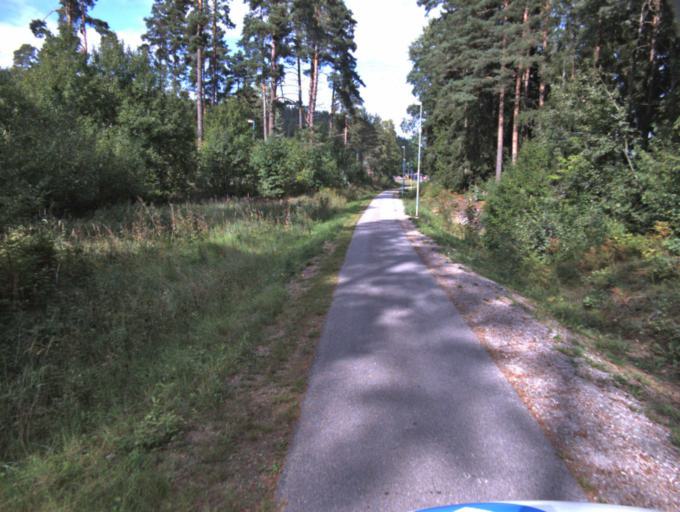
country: SE
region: Vaestra Goetaland
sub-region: Ulricehamns Kommun
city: Ulricehamn
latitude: 57.8172
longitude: 13.4119
